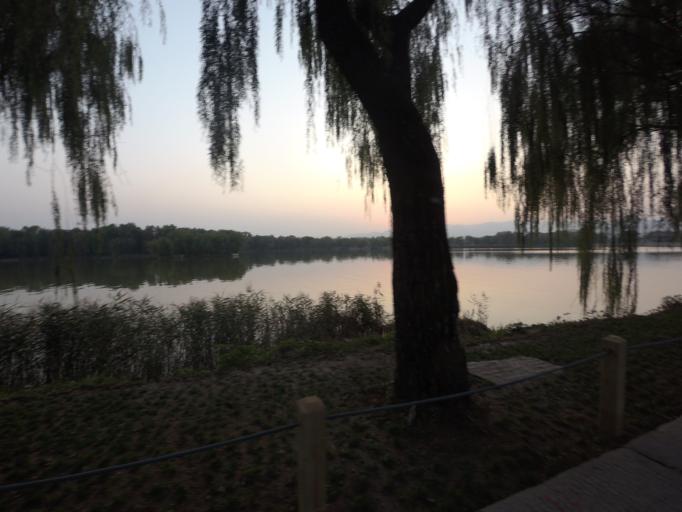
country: CN
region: Beijing
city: Haidian
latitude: 39.9830
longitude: 116.2722
